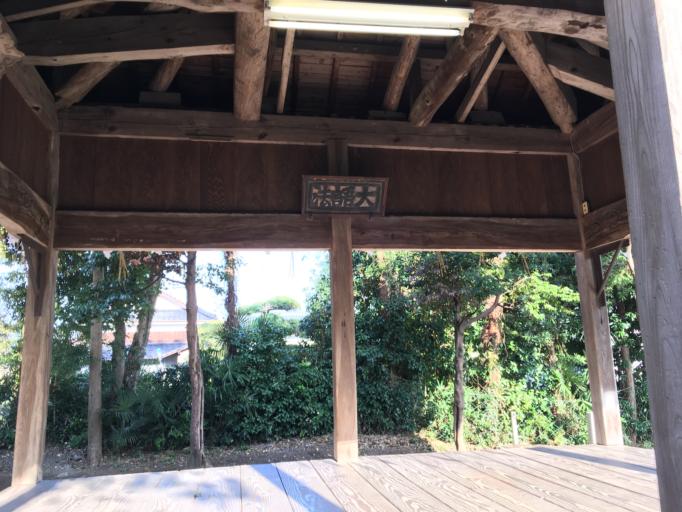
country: JP
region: Fukuoka
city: Nakatsu
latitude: 33.5716
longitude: 131.2226
